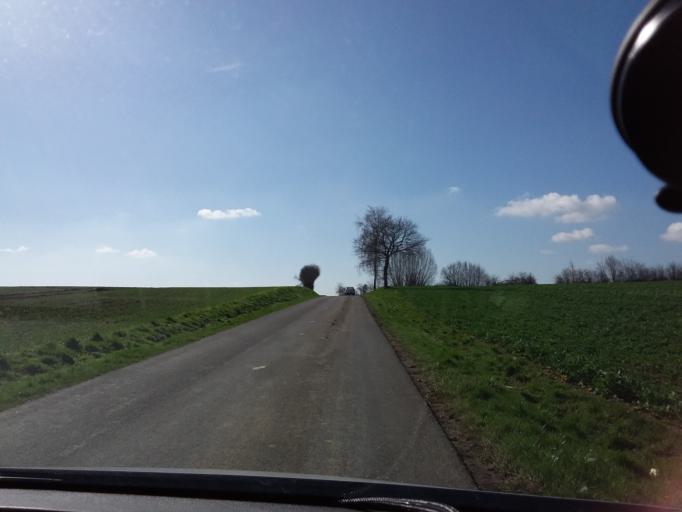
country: FR
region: Picardie
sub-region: Departement de l'Aisne
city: Hirson
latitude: 49.8938
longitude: 4.0979
